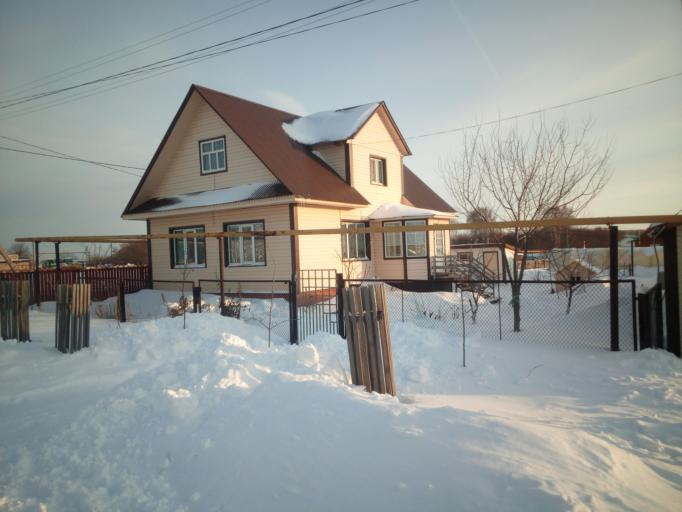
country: RU
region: Bashkortostan
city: Amzya
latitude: 56.1673
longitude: 54.3787
